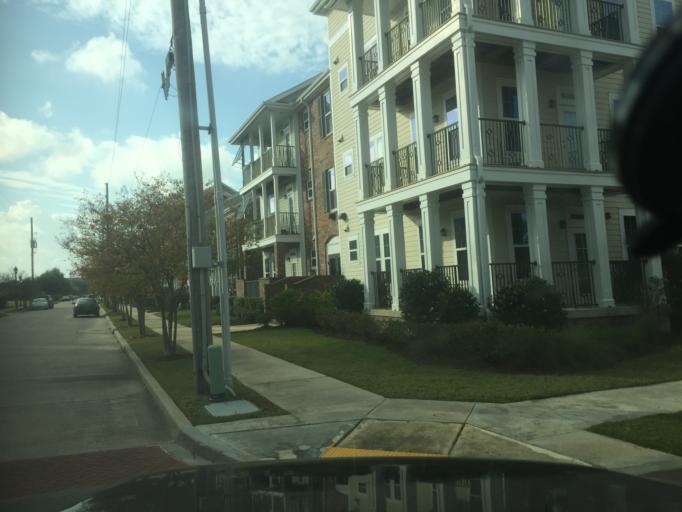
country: US
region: Louisiana
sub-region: Orleans Parish
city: New Orleans
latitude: 29.9980
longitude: -90.0761
